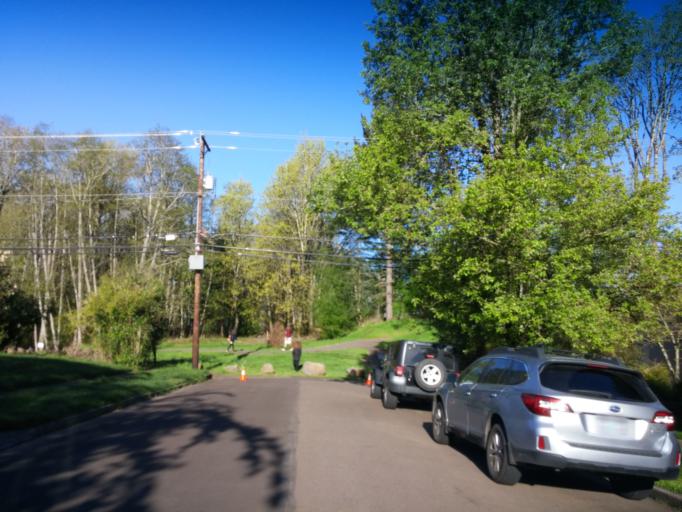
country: US
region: Oregon
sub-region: Washington County
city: West Slope
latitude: 45.5040
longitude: -122.7795
